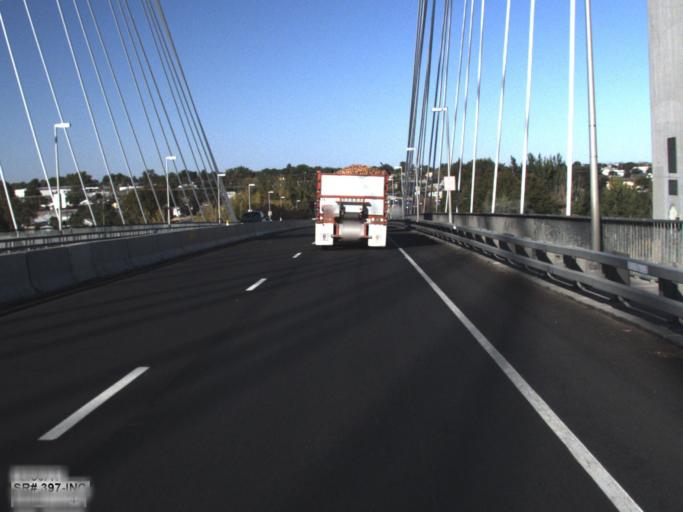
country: US
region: Washington
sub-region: Franklin County
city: Pasco
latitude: 46.2197
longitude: -119.1039
